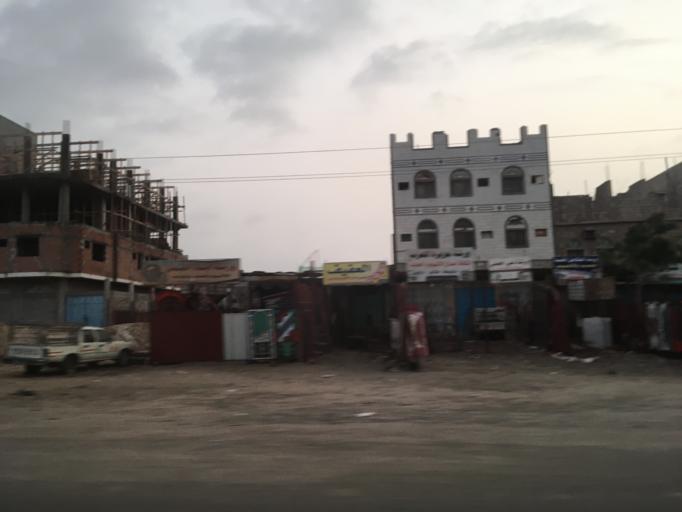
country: YE
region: Lahij
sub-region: Al  Hawtah
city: Lahij
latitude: 13.0053
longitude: 44.9111
